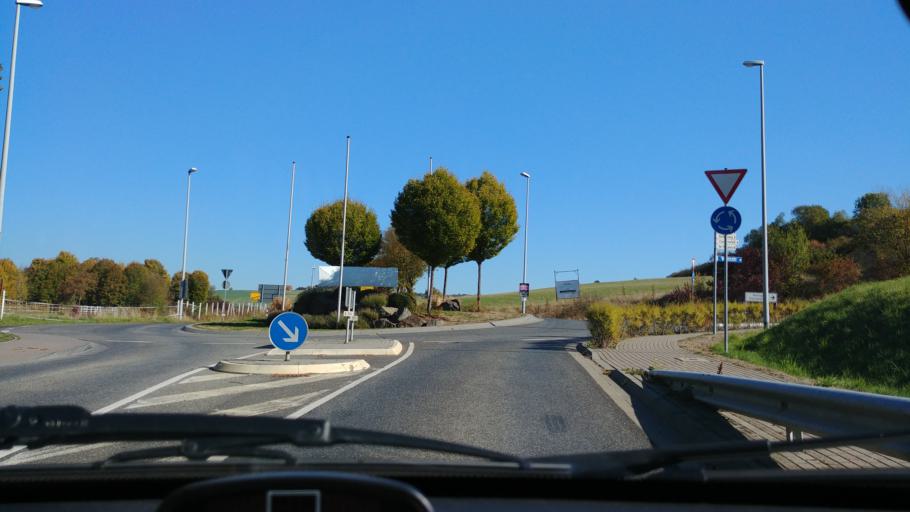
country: DE
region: Rheinland-Pfalz
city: Katzenelnbogen
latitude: 50.2691
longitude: 7.9829
